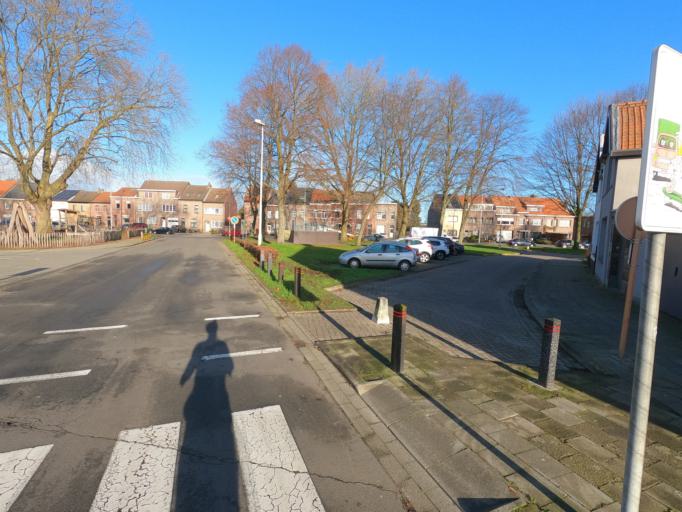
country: BE
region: Flanders
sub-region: Provincie Antwerpen
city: Wijnegem
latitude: 51.2289
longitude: 4.5122
